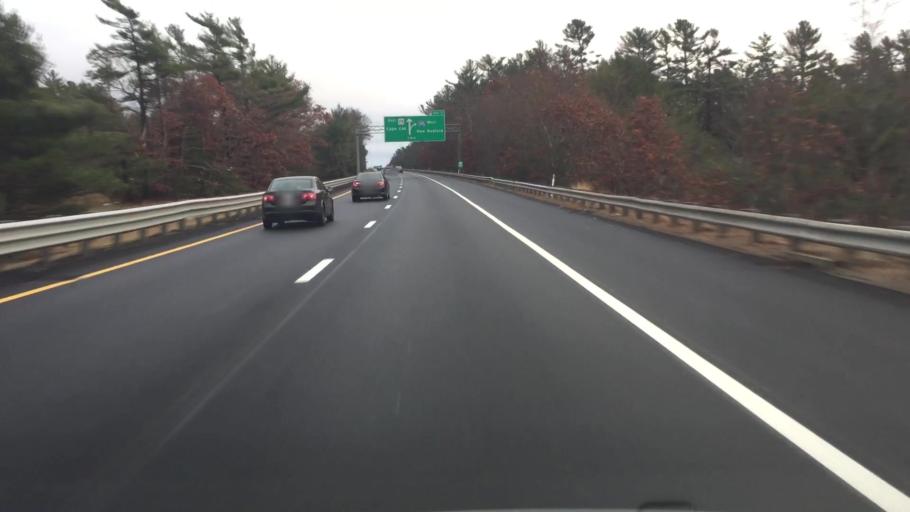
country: US
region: Massachusetts
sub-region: Plymouth County
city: West Wareham
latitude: 41.7958
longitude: -70.7547
